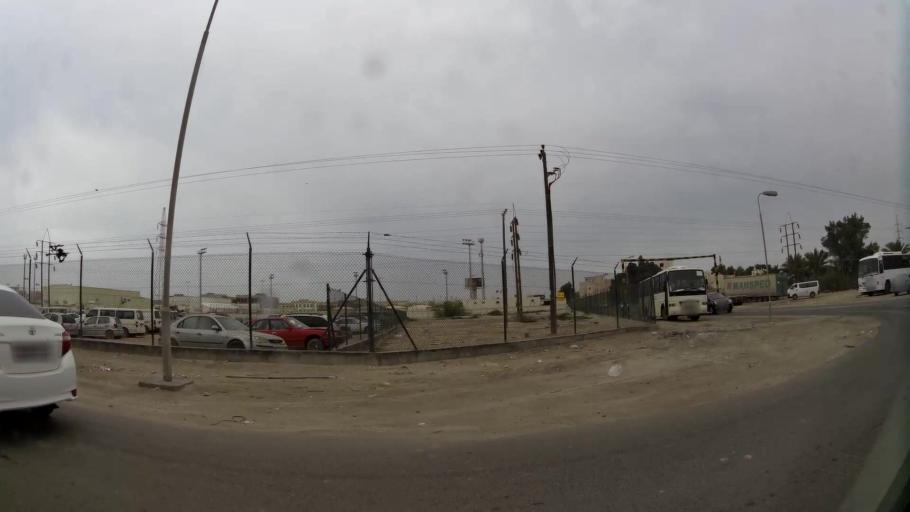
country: BH
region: Northern
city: Madinat `Isa
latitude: 26.1763
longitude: 50.5347
